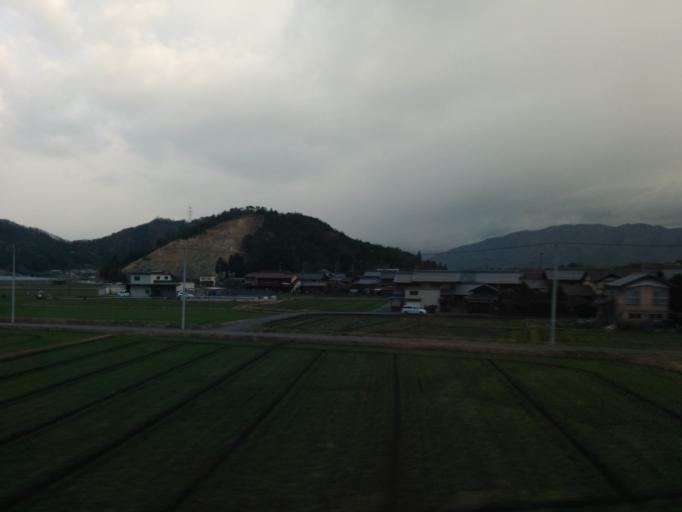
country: JP
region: Shiga Prefecture
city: Nagahama
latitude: 35.3623
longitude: 136.3454
